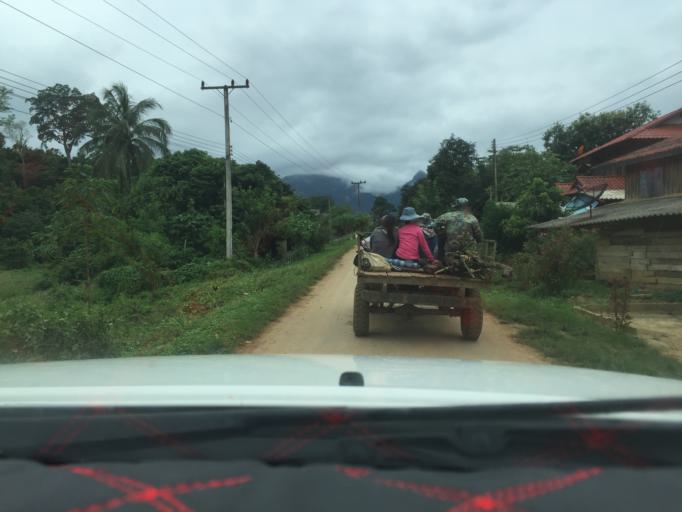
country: TH
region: Phayao
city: Phu Sang
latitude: 19.7707
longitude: 100.5421
